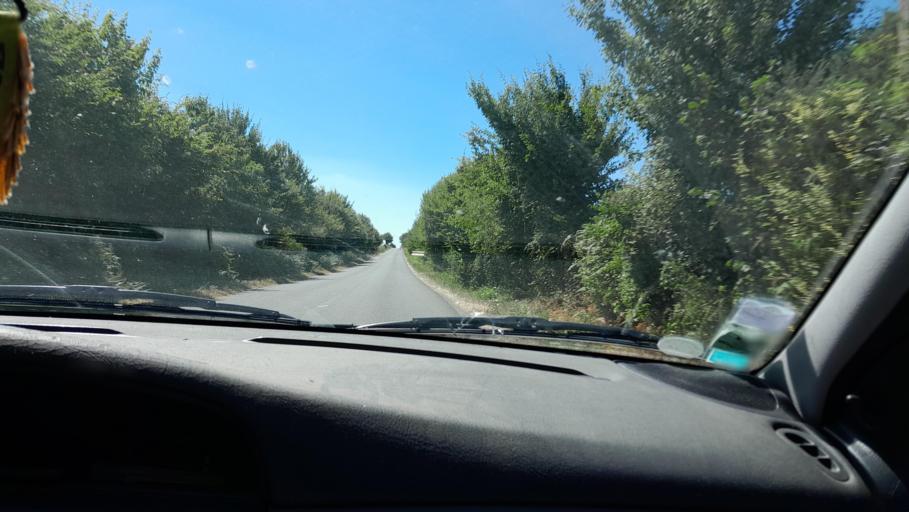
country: FR
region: Pays de la Loire
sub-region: Departement de la Mayenne
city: Congrier
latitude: 47.8365
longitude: -1.1571
